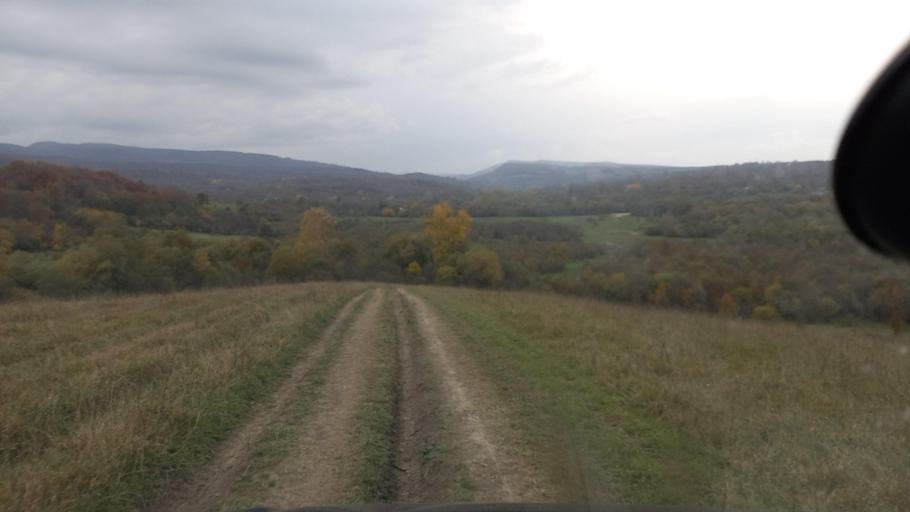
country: RU
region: Krasnodarskiy
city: Gubskaya
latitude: 44.2938
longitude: 40.5559
